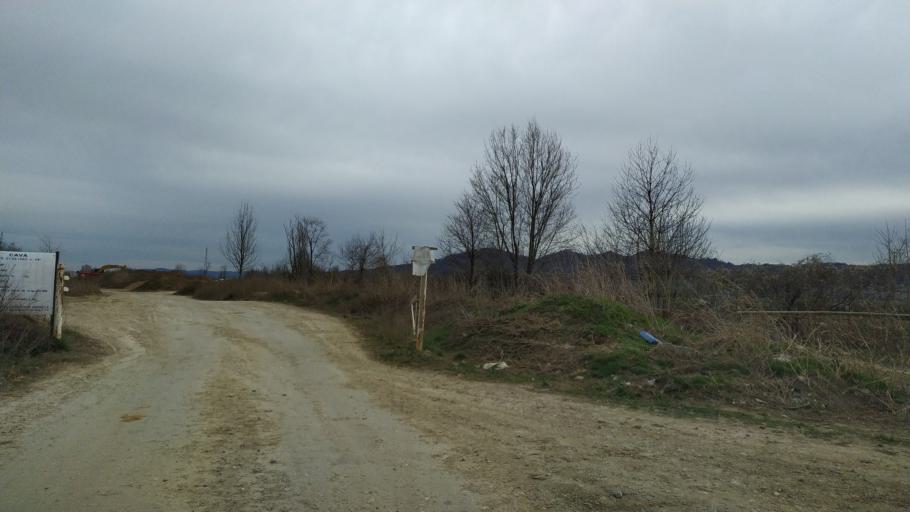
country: IT
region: Veneto
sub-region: Provincia di Vicenza
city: Malo
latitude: 45.6531
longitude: 11.4362
